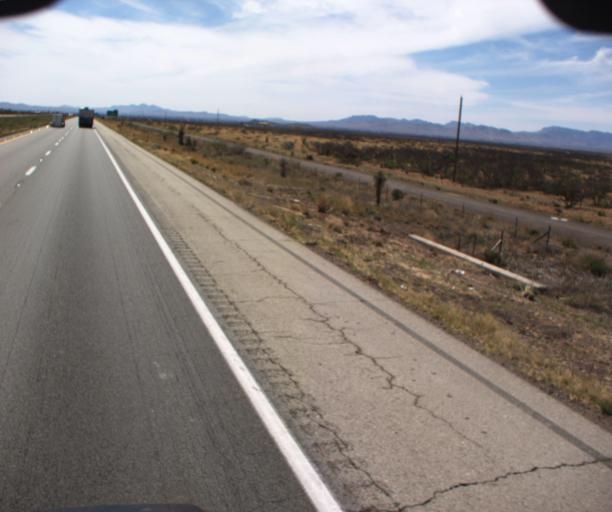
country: US
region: Arizona
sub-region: Cochise County
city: Willcox
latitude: 32.3256
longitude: -109.7746
